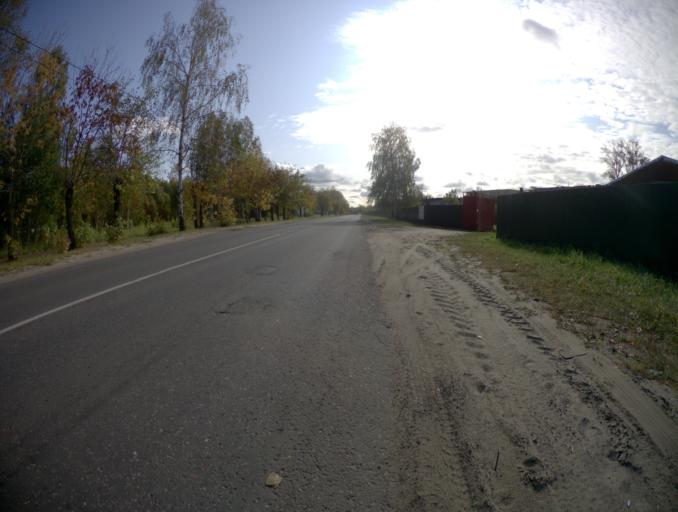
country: RU
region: Moskovskaya
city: Roshal'
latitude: 55.6615
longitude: 39.8732
